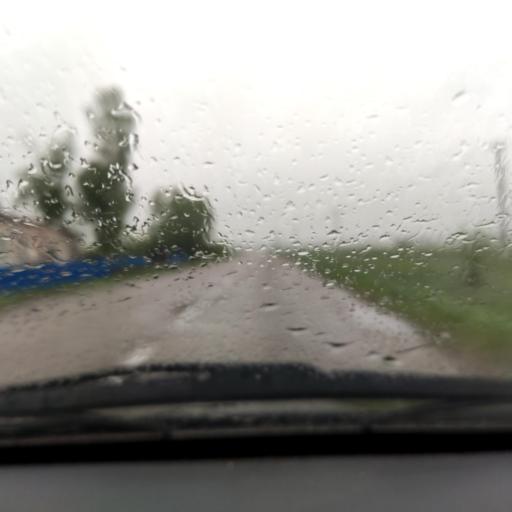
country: RU
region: Bashkortostan
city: Asanovo
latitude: 54.7758
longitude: 55.4940
